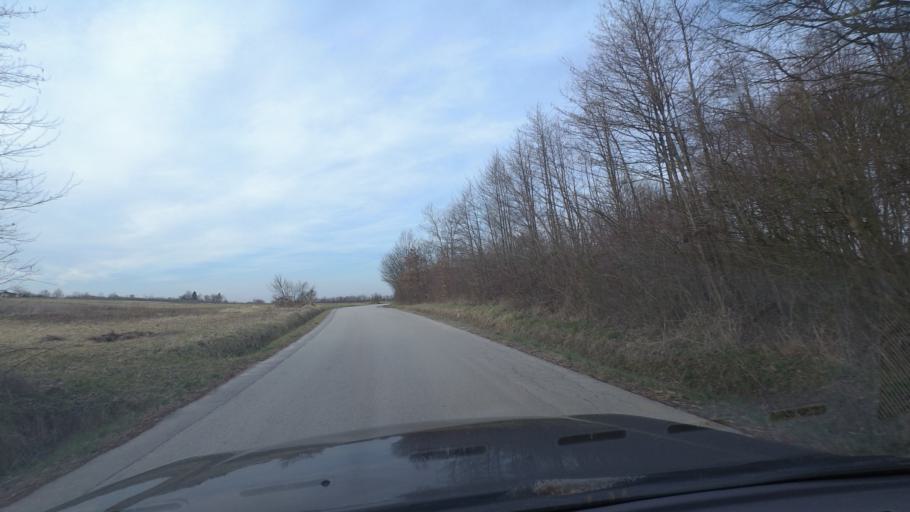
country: HR
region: Grad Zagreb
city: Horvati
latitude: 45.7099
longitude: 15.8260
